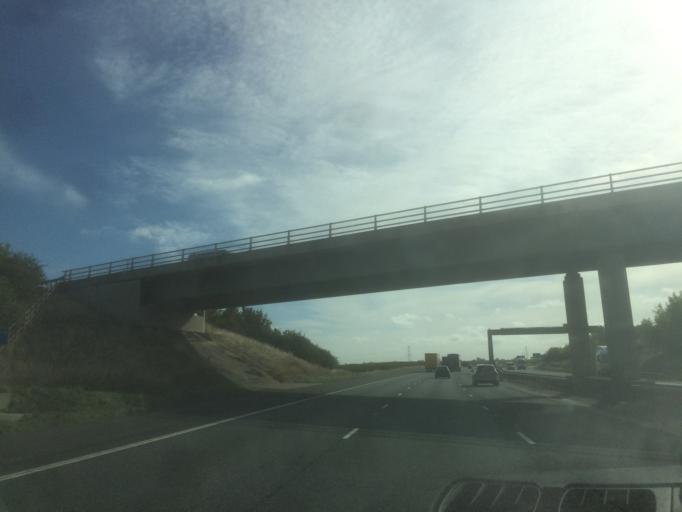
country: GB
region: England
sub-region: City and Borough of Leeds
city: Ledsham
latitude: 53.7780
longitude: -1.2994
